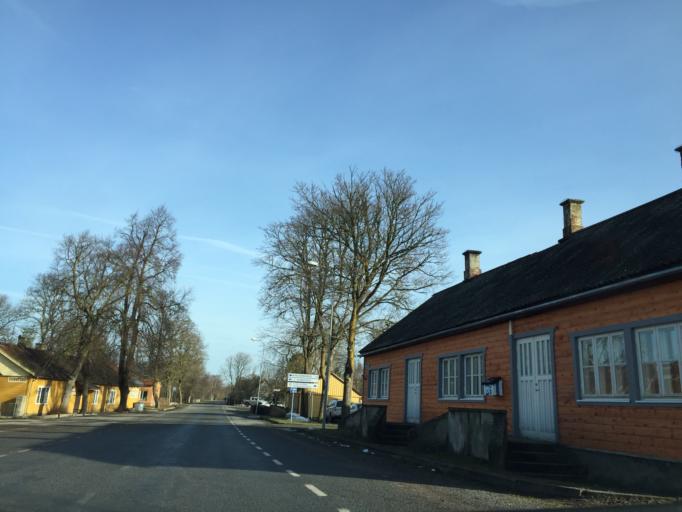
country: EE
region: Saare
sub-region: Kuressaare linn
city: Kuressaare
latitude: 58.3597
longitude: 22.0381
